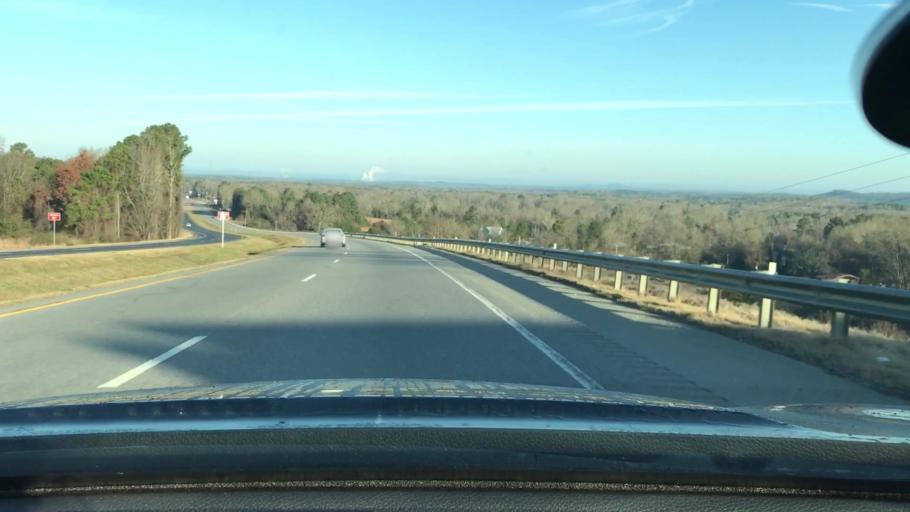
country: US
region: Alabama
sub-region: Talladega County
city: Mignon
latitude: 33.2041
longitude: -86.3077
